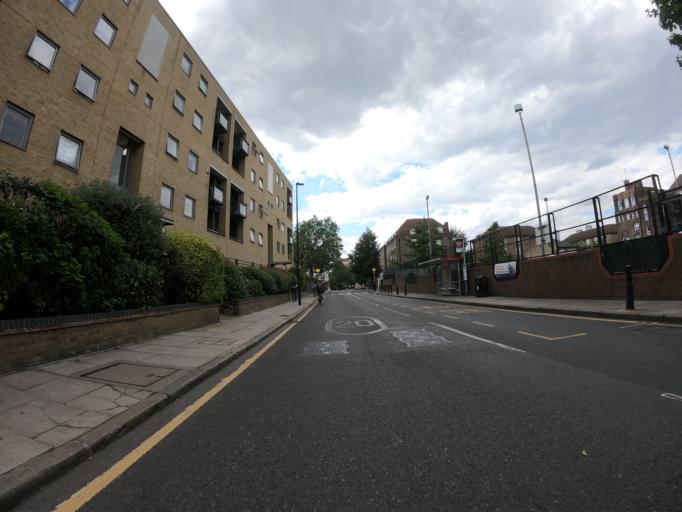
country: GB
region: England
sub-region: Greater London
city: Poplar
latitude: 51.4888
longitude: -0.0200
